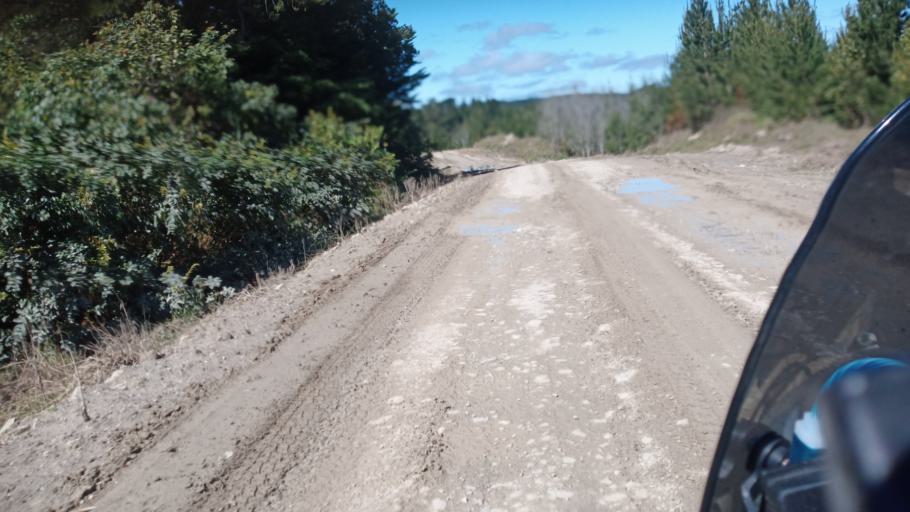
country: NZ
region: Gisborne
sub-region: Gisborne District
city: Gisborne
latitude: -38.8870
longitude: 177.7860
